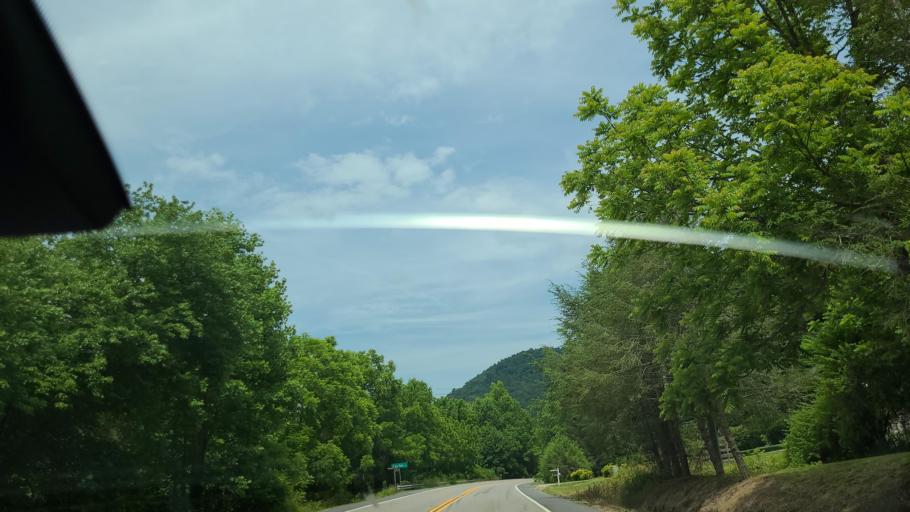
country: US
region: North Carolina
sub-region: Macon County
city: Franklin
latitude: 35.1386
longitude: -83.2842
